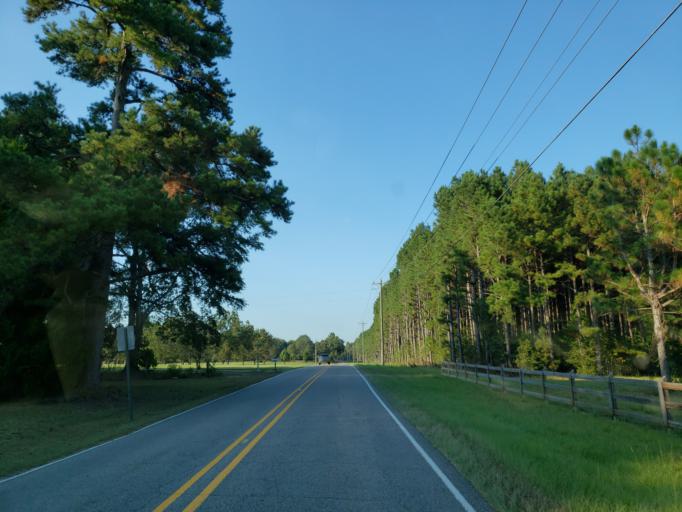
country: US
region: Mississippi
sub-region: Lamar County
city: West Hattiesburg
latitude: 31.3050
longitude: -89.4449
